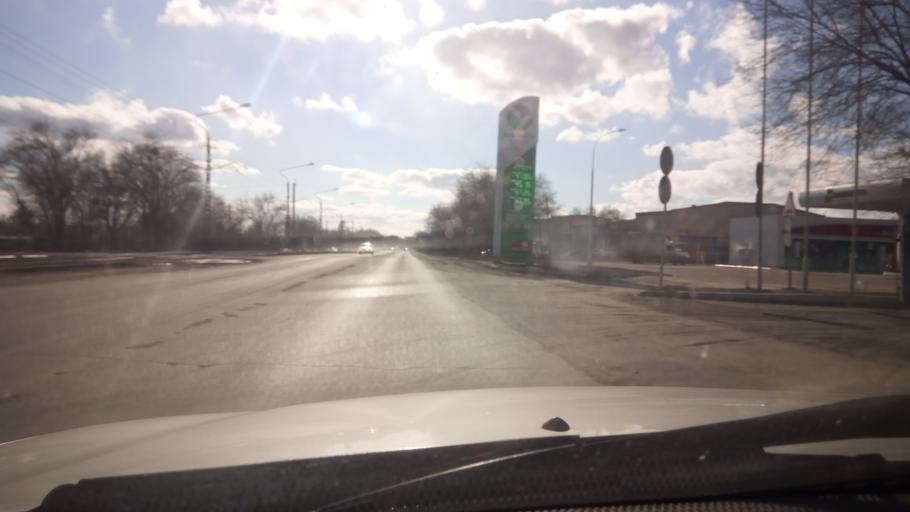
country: RU
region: Orenburg
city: Novotroitsk
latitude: 51.2065
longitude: 58.3602
